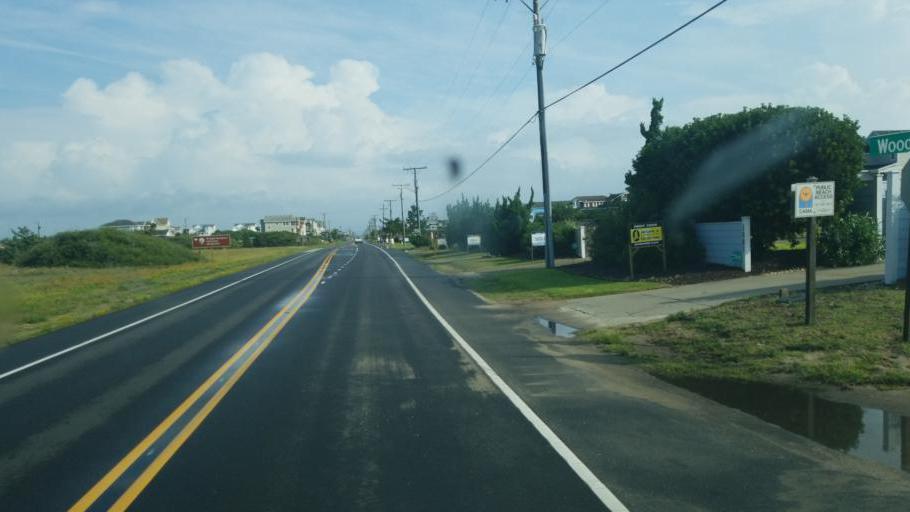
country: US
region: North Carolina
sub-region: Dare County
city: Kill Devil Hills
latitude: 36.0205
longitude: -75.6612
